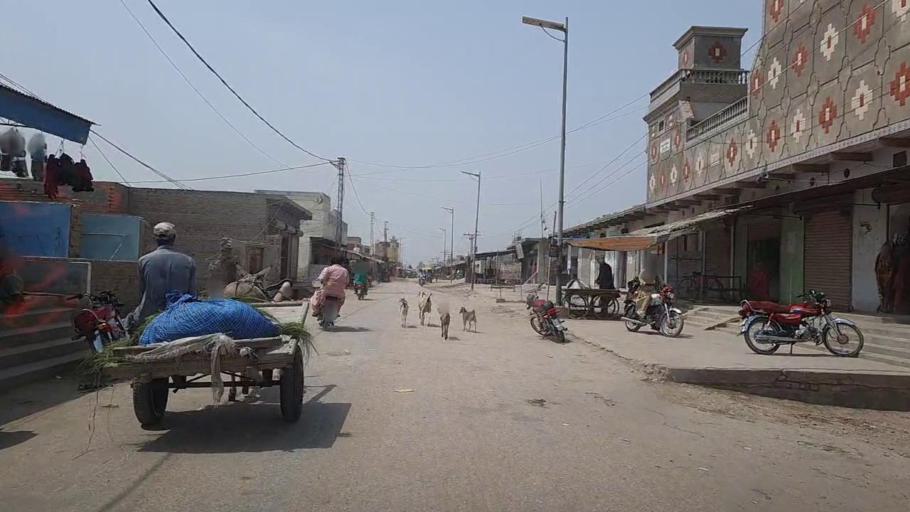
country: PK
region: Sindh
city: Radhan
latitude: 27.1723
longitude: 67.9473
